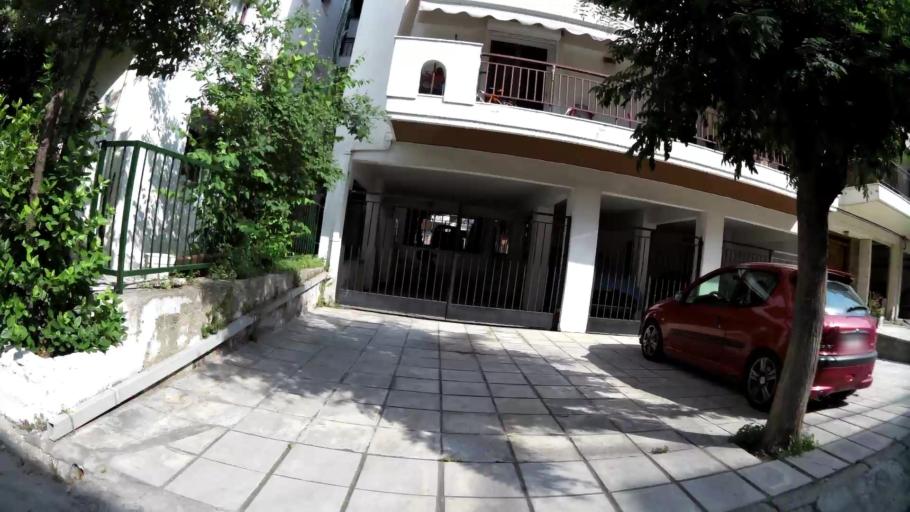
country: GR
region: Central Macedonia
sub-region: Nomos Thessalonikis
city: Stavroupoli
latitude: 40.6710
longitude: 22.9292
